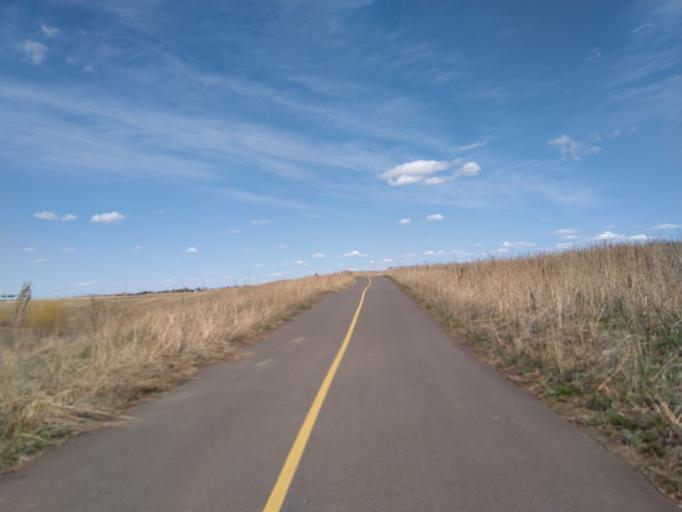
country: CA
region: Alberta
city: Chestermere
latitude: 51.0172
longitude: -113.9271
